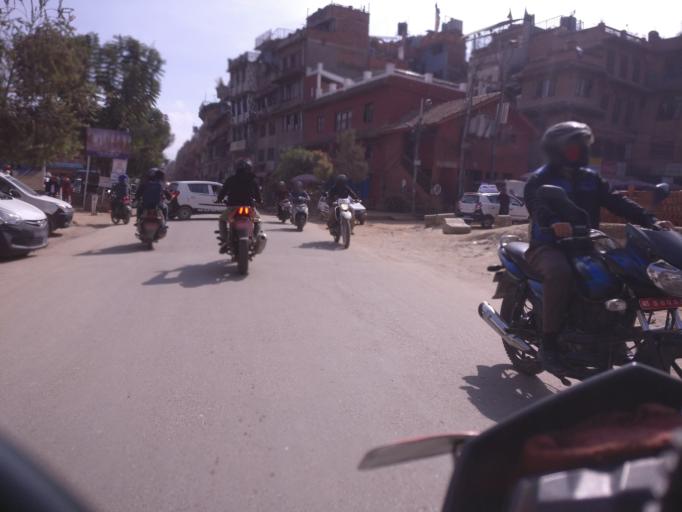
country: NP
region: Central Region
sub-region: Bagmati Zone
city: Patan
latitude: 27.6724
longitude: 85.3251
